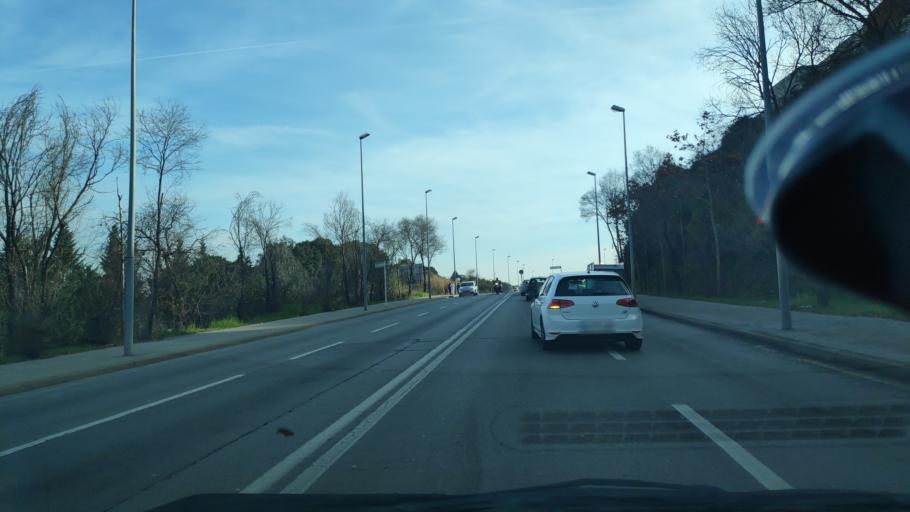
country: ES
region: Catalonia
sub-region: Provincia de Barcelona
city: Sabadell
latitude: 41.5685
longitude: 2.0990
